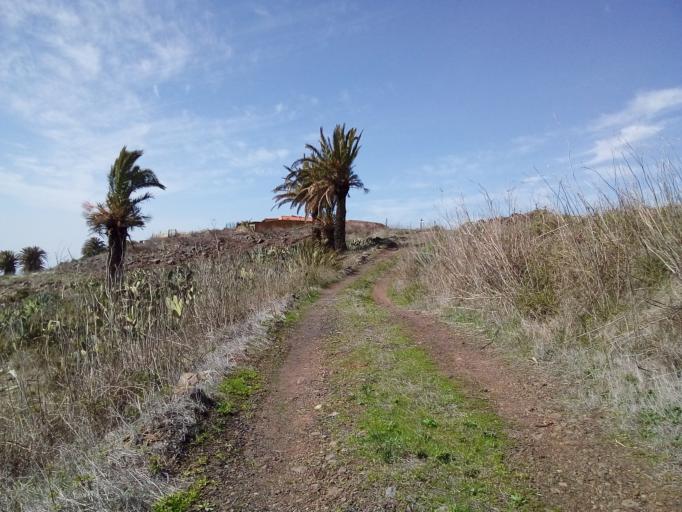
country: ES
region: Canary Islands
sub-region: Provincia de Santa Cruz de Tenerife
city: Vallehermosa
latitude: 28.1177
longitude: -17.2898
